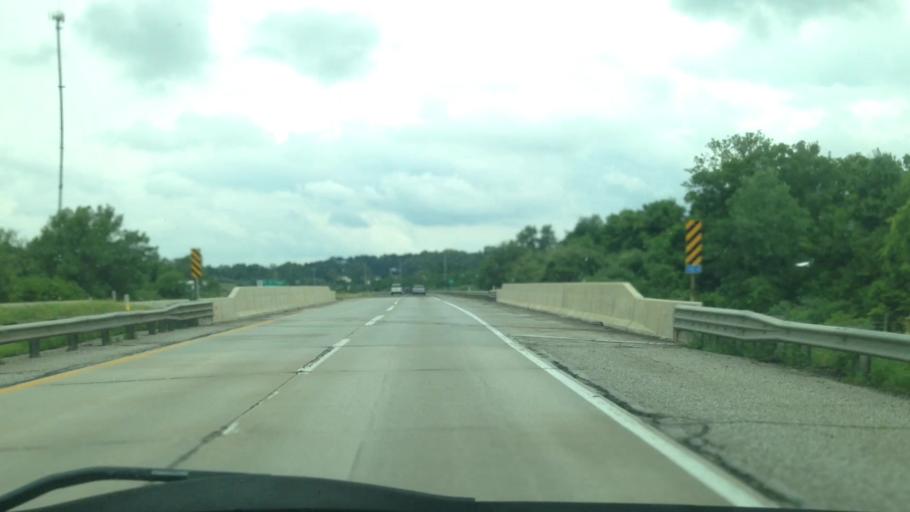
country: US
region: Indiana
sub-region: Steuben County
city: Fremont
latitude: 41.7440
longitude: -85.0191
